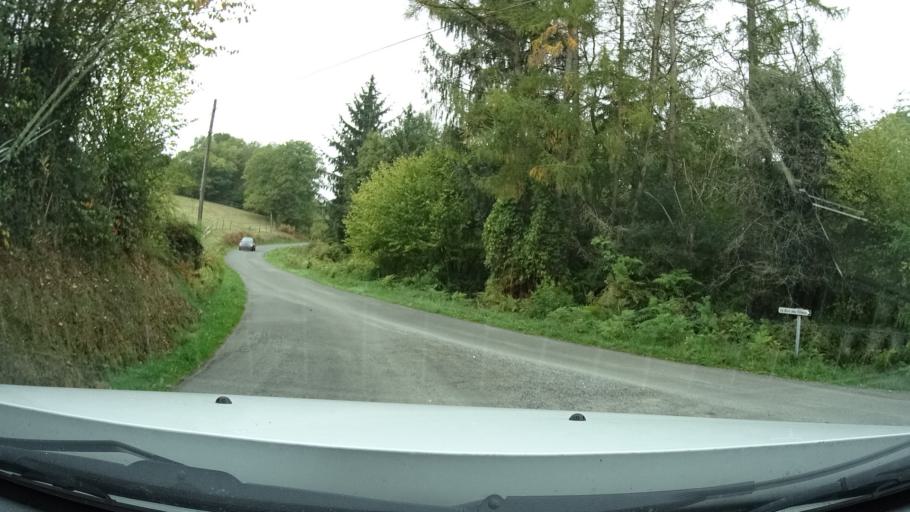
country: FR
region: Aquitaine
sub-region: Departement de la Dordogne
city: La Coquille
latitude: 45.5136
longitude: 0.9348
